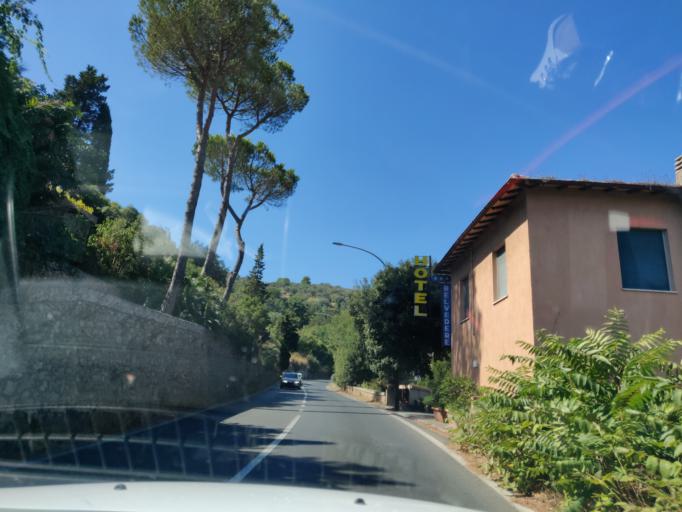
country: IT
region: Tuscany
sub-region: Provincia di Grosseto
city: Monte Argentario
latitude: 42.4376
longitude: 11.1327
